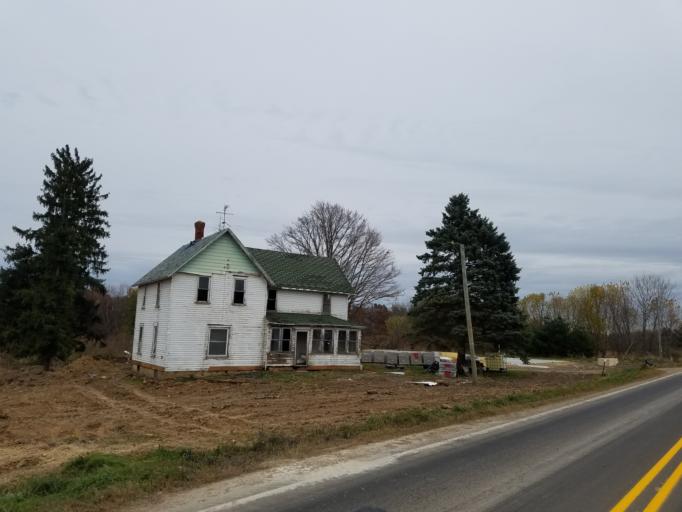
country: US
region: Wisconsin
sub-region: Vernon County
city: Hillsboro
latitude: 43.5894
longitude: -90.3407
